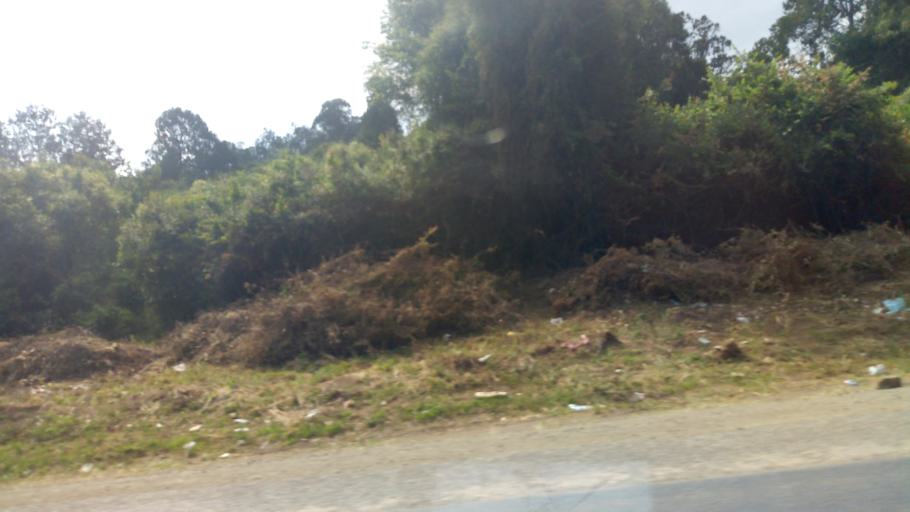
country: KE
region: Kiambu
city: Limuru
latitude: -1.0755
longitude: 36.6022
